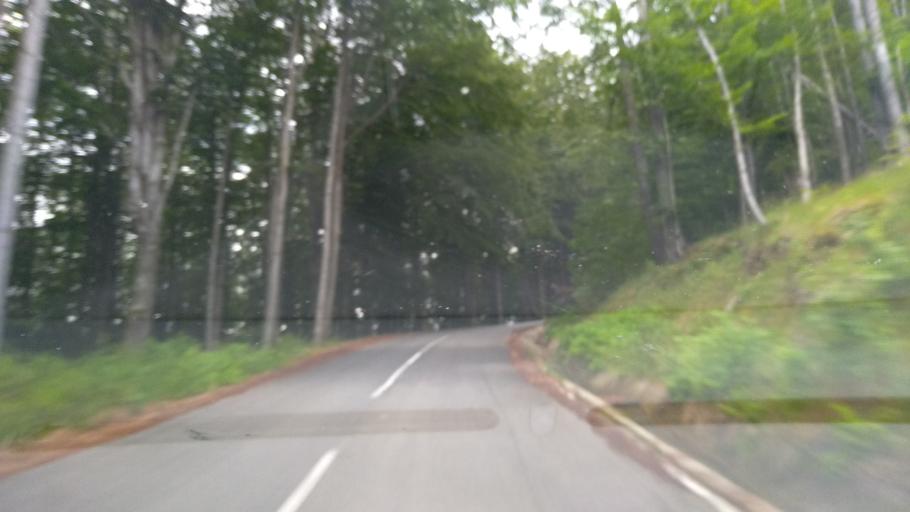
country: RO
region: Hunedoara
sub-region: Municipiul  Vulcan
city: Jiu-Paroseni
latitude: 45.3362
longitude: 23.2915
